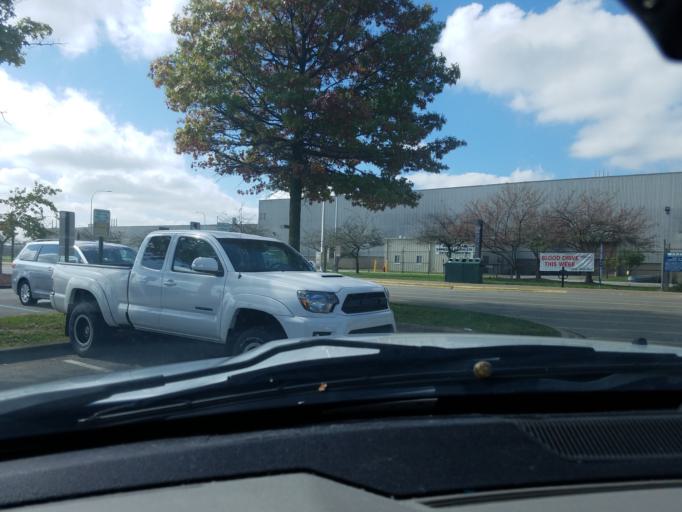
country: US
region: Kentucky
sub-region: Scott County
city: Georgetown
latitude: 38.2536
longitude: -84.5316
